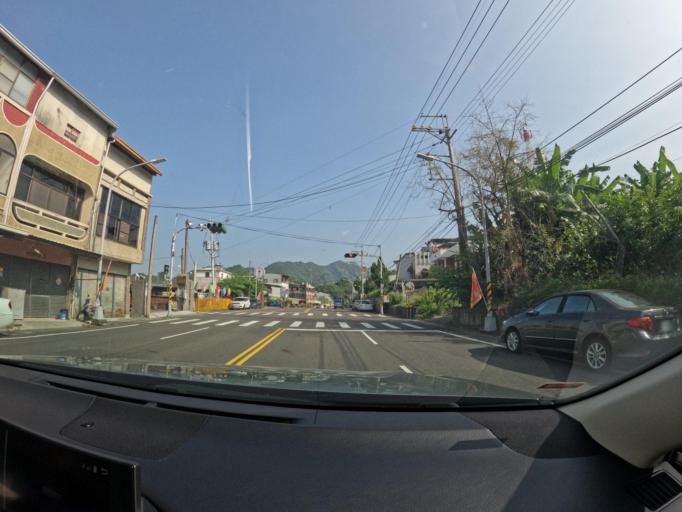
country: TW
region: Taiwan
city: Yujing
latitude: 23.0746
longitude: 120.5194
